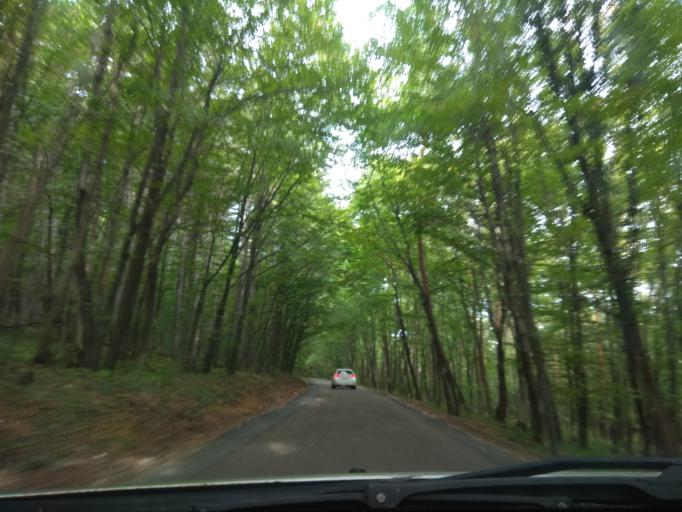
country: HU
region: Borsod-Abauj-Zemplen
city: Sajobabony
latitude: 48.0695
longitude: 20.6691
